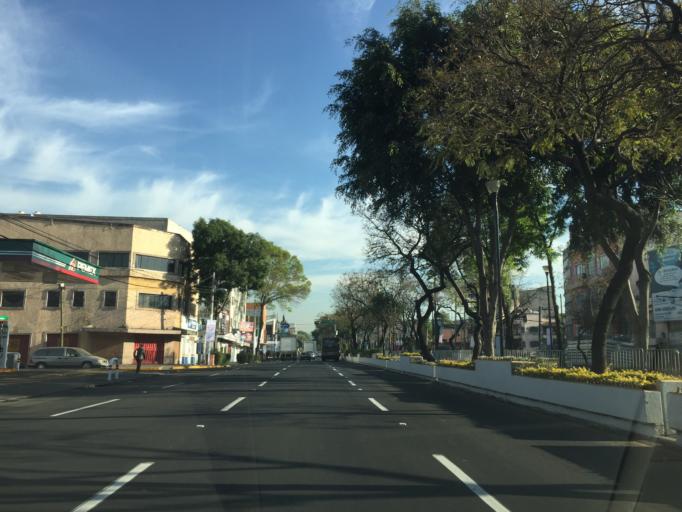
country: MX
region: Mexico
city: Colonia Lindavista
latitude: 19.4669
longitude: -99.1242
